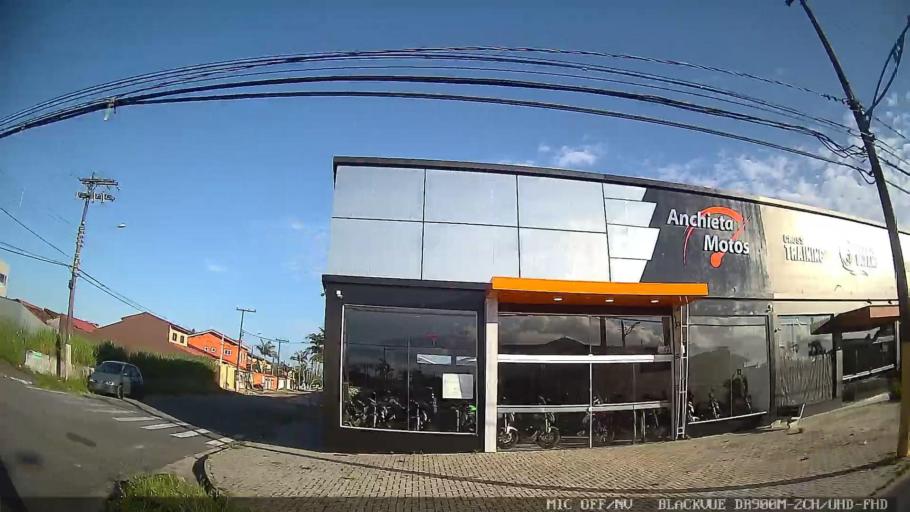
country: BR
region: Sao Paulo
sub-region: Peruibe
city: Peruibe
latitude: -24.2973
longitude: -46.9700
